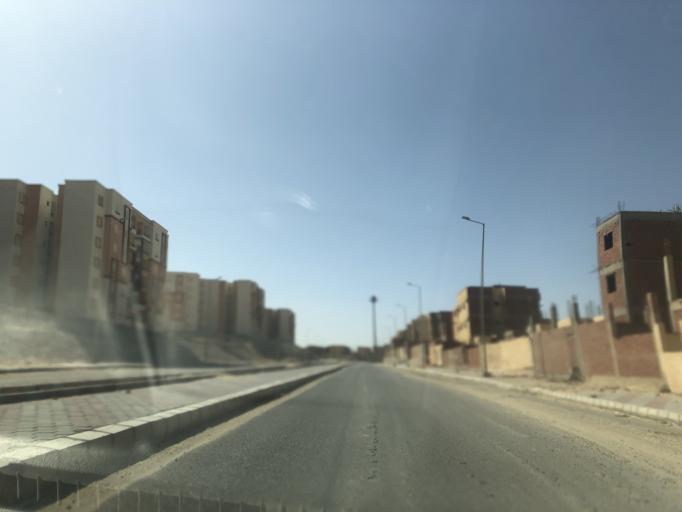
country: EG
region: Al Jizah
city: Madinat Sittah Uktubar
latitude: 29.9345
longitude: 30.9807
